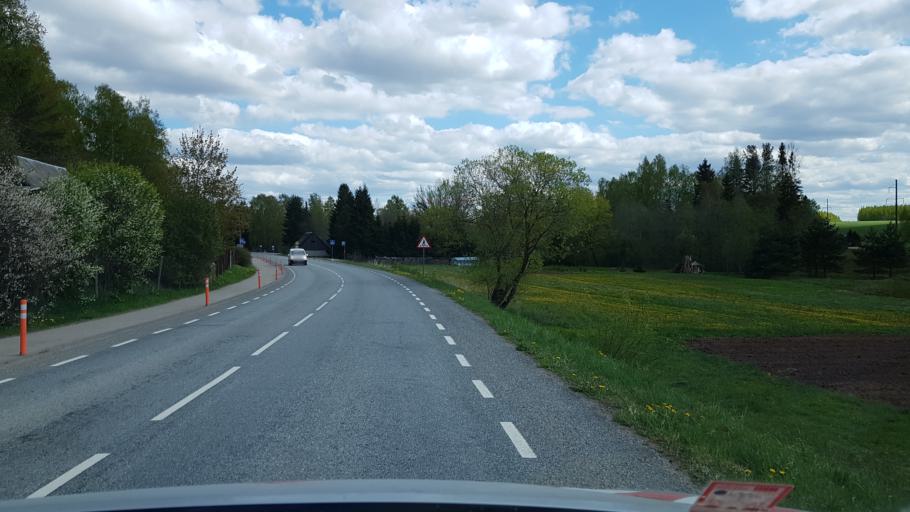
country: EE
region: Tartu
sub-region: UElenurme vald
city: Ulenurme
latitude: 58.2944
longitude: 26.8891
